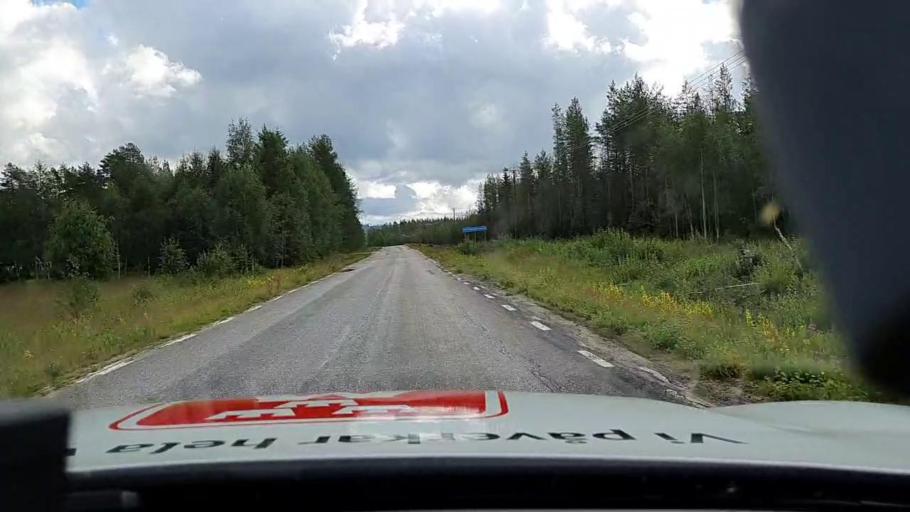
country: SE
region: Norrbotten
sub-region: Overkalix Kommun
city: OEverkalix
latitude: 66.2472
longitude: 22.9032
